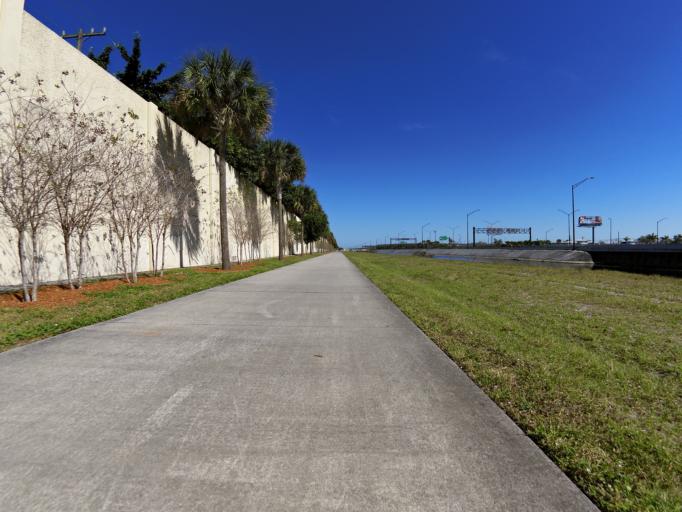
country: US
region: Florida
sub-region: Broward County
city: Pine Island Ridge
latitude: 26.1092
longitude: -80.2876
